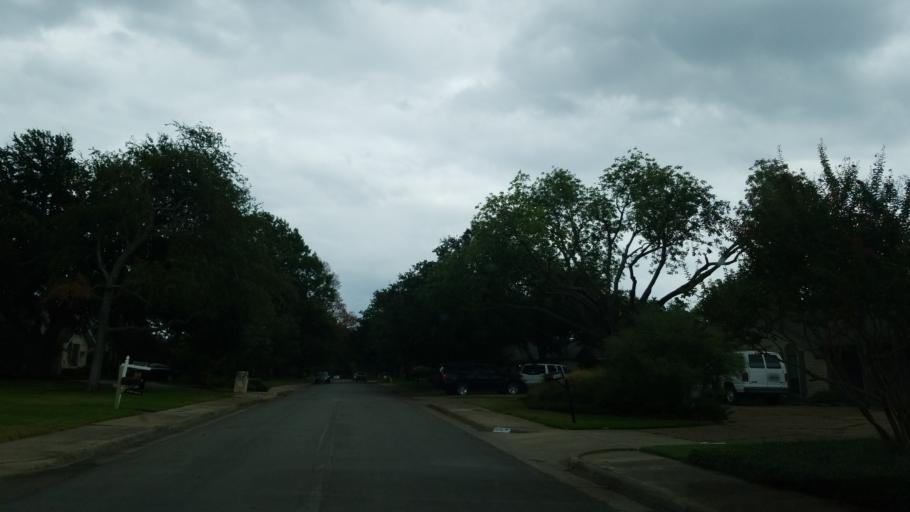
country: US
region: Texas
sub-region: Dallas County
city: Richardson
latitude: 32.9469
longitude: -96.7754
